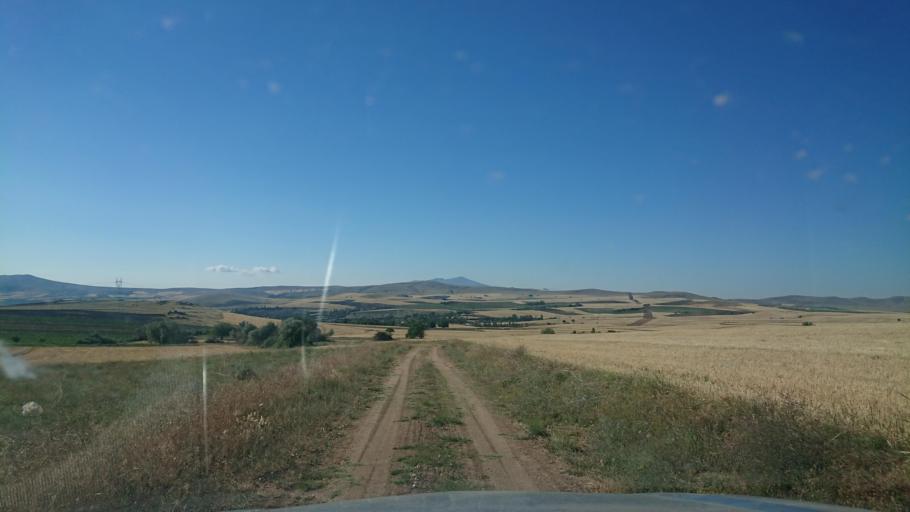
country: TR
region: Aksaray
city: Agacoren
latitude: 38.8349
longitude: 33.9387
